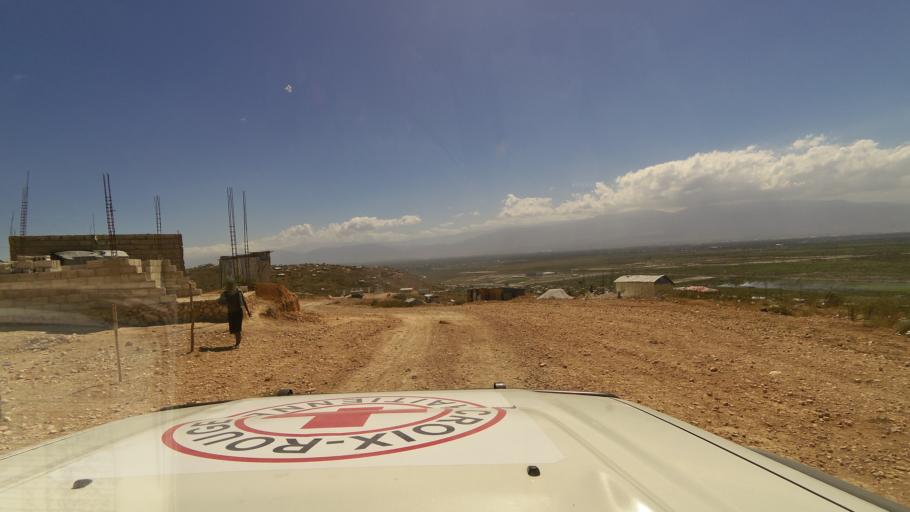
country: HT
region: Ouest
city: Croix des Bouquets
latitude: 18.6706
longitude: -72.2949
